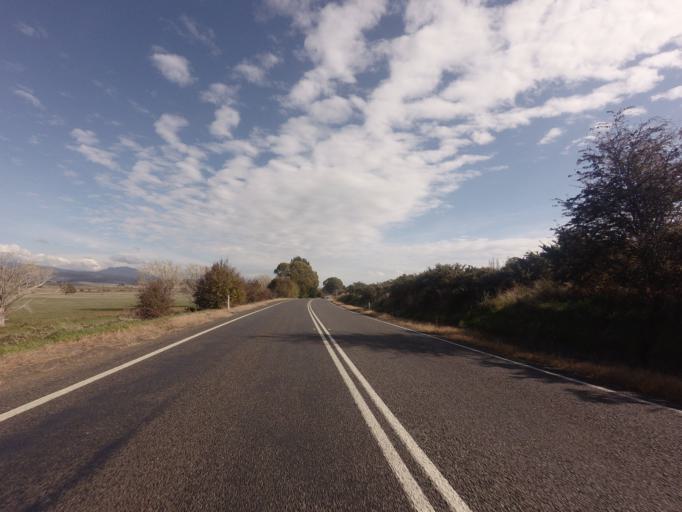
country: AU
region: Tasmania
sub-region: Meander Valley
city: Westbury
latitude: -41.5264
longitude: 146.8161
